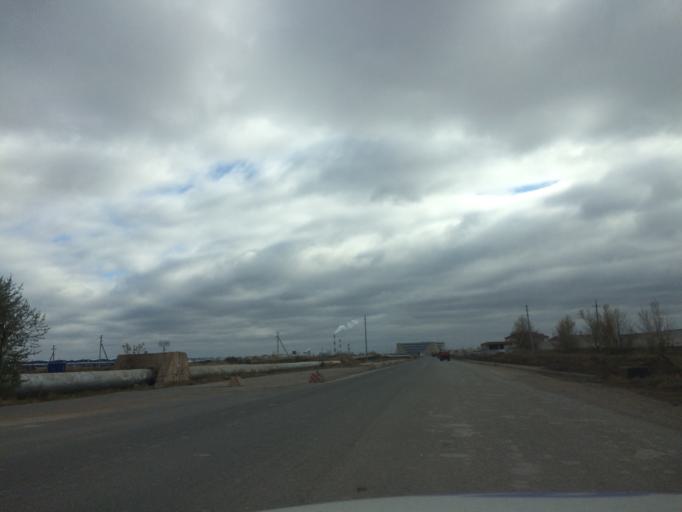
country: KZ
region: Astana Qalasy
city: Astana
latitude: 51.2066
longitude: 71.4531
